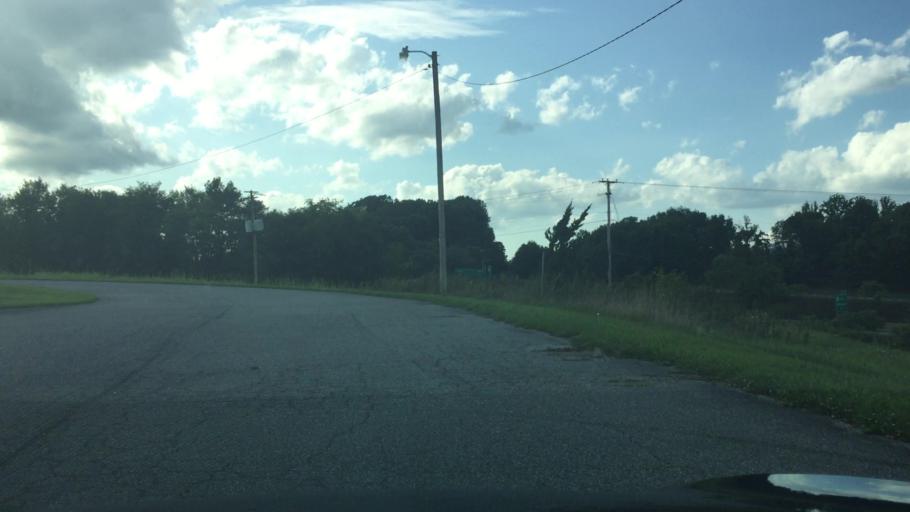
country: US
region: Virginia
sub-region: Wythe County
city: Wytheville
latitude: 36.9445
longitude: -81.0457
